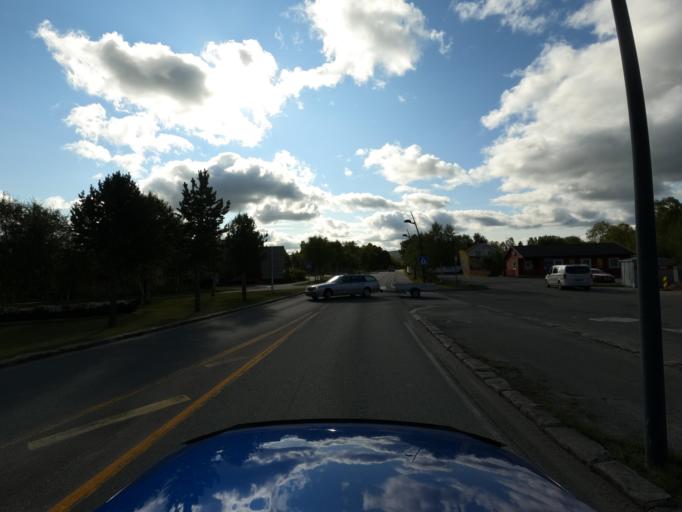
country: NO
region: Finnmark Fylke
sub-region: Karasjok
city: Karasjohka
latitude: 69.4717
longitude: 25.5108
